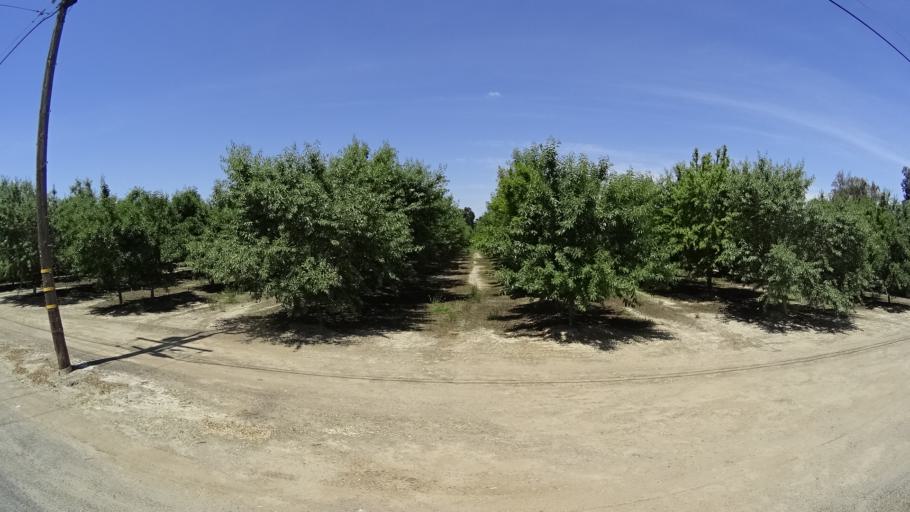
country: US
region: California
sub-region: Kings County
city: Lemoore
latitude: 36.2837
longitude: -119.7645
